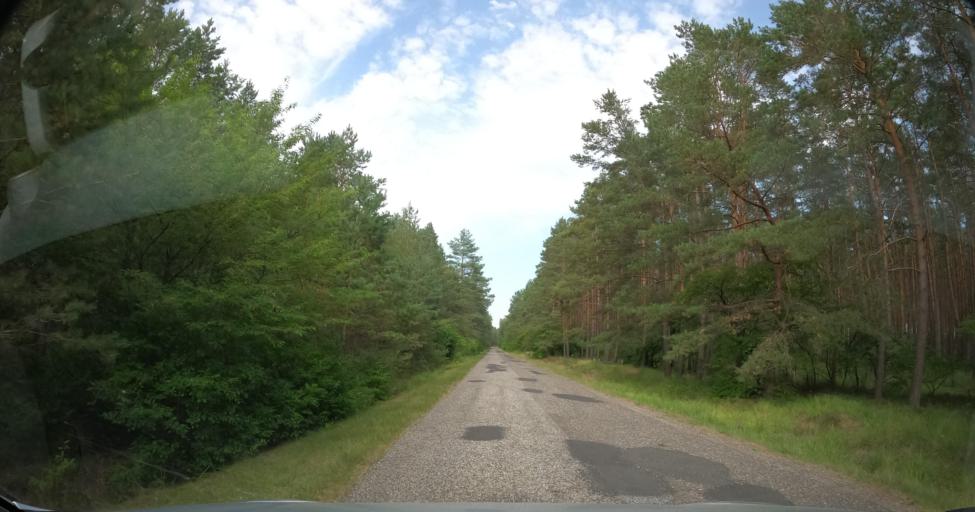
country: PL
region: West Pomeranian Voivodeship
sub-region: Powiat goleniowski
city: Goleniow
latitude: 53.4697
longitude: 14.8314
